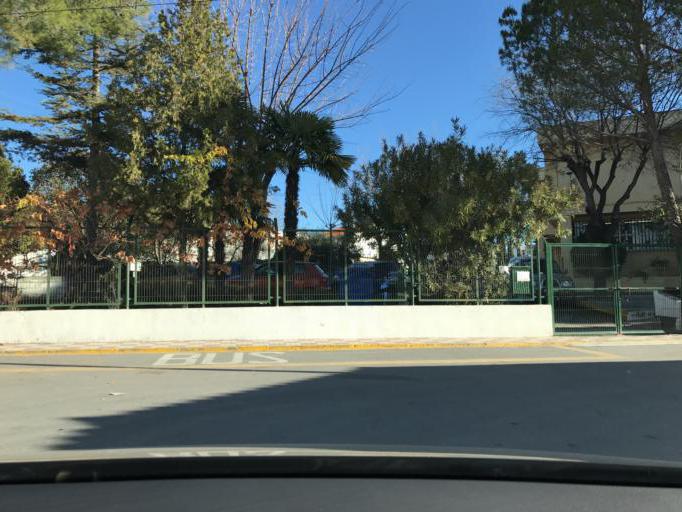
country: ES
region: Andalusia
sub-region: Provincia de Granada
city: Albolote
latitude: 37.2360
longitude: -3.6588
